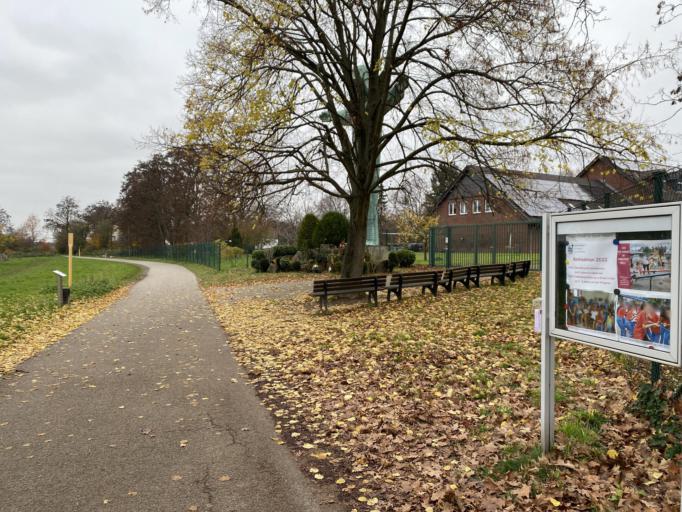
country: DE
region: North Rhine-Westphalia
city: Sankt Augustin
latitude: 50.7737
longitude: 7.1749
